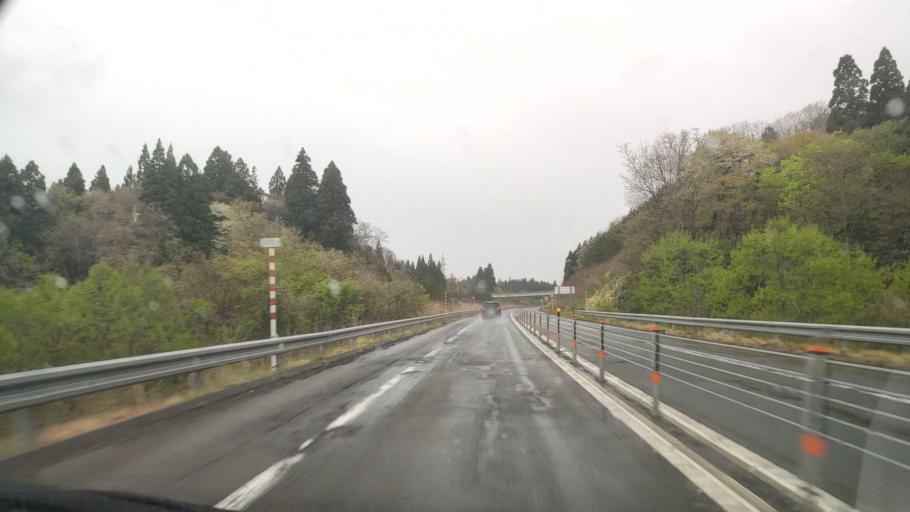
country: JP
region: Akita
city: Noshiromachi
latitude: 40.1700
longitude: 140.0523
